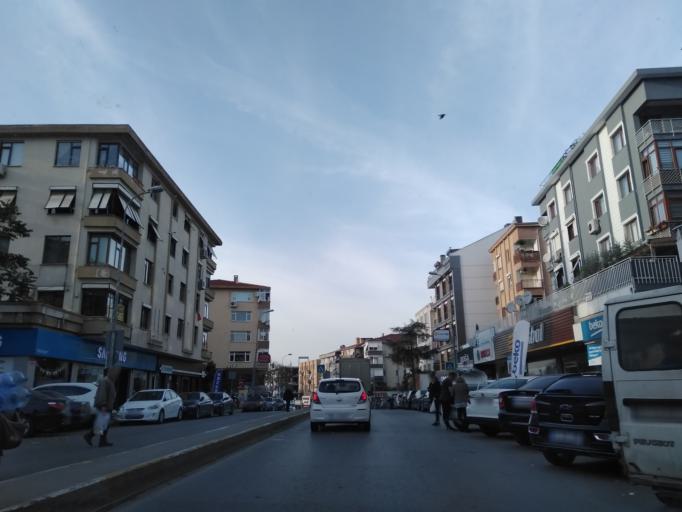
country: TR
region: Istanbul
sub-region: Atasehir
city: Atasehir
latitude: 40.9482
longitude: 29.1066
